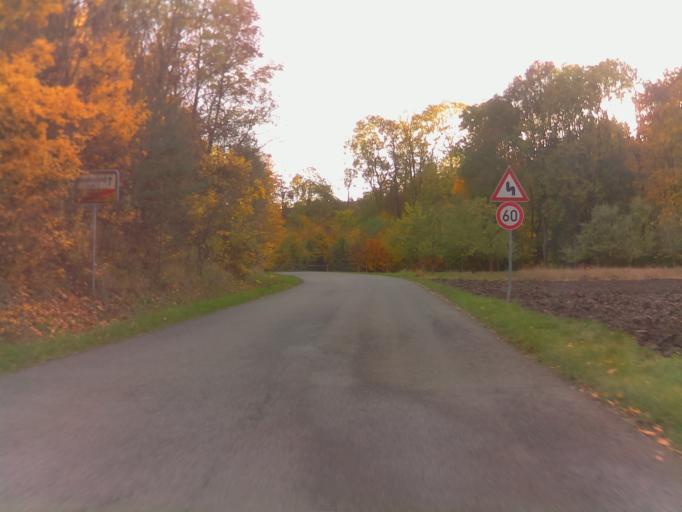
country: DE
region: Thuringia
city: Blankenhain
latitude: 50.8494
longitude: 11.3608
